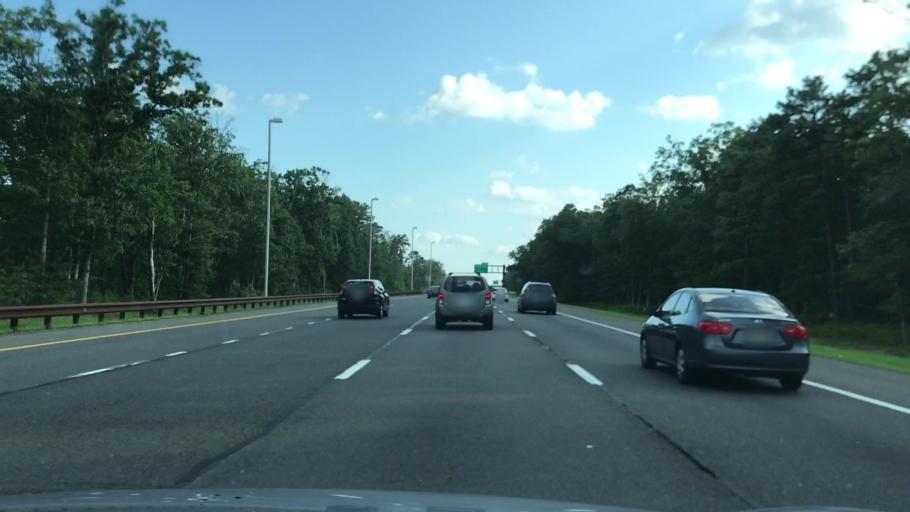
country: US
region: New Jersey
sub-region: Ocean County
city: Forked River
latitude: 39.8704
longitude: -74.2169
